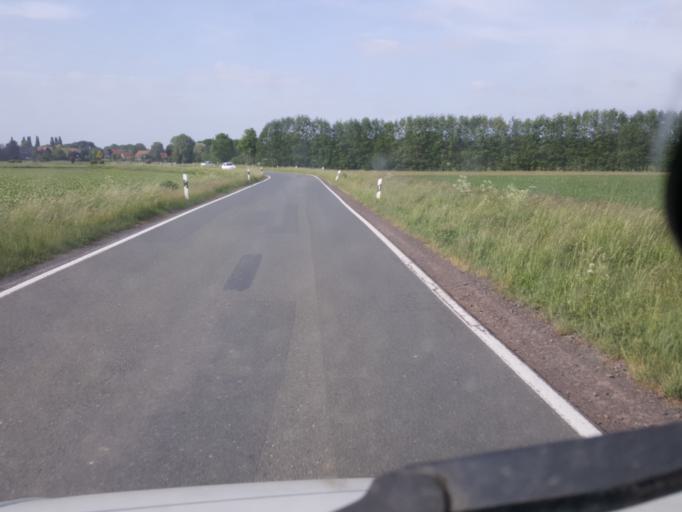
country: DE
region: North Rhine-Westphalia
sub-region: Regierungsbezirk Detmold
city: Minden
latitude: 52.3459
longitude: 8.8476
